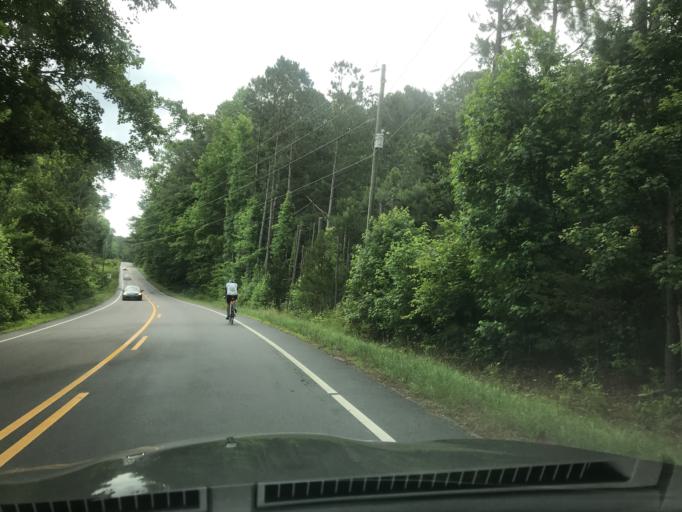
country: US
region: North Carolina
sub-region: Wake County
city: Knightdale
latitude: 35.8356
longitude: -78.4886
